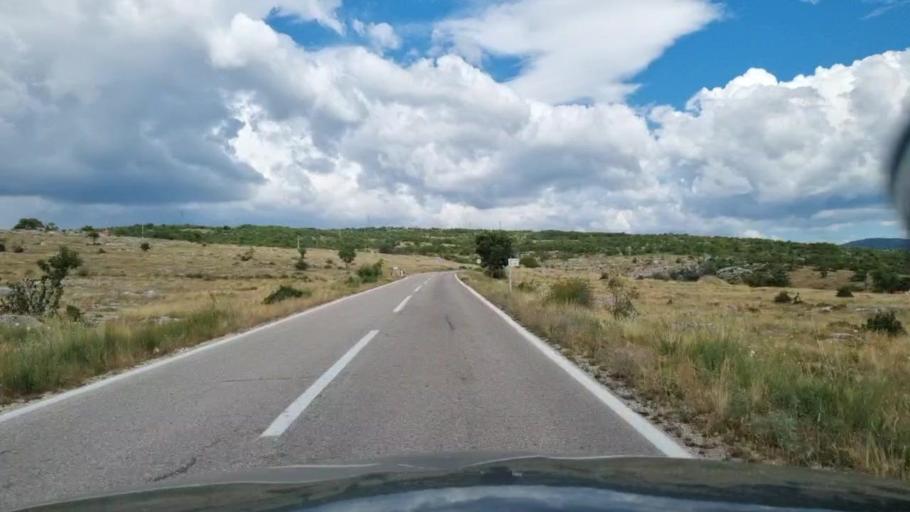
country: BA
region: Federation of Bosnia and Herzegovina
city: Blagaj
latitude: 43.2509
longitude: 17.9544
